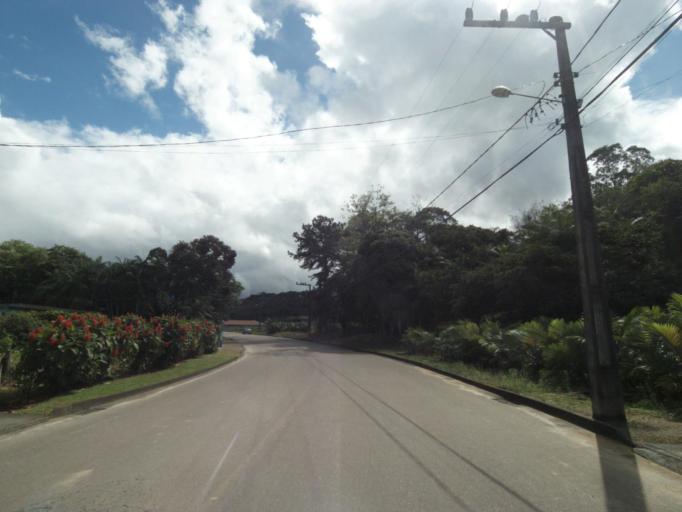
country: BR
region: Santa Catarina
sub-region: Pomerode
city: Pomerode
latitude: -26.6828
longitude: -49.1757
